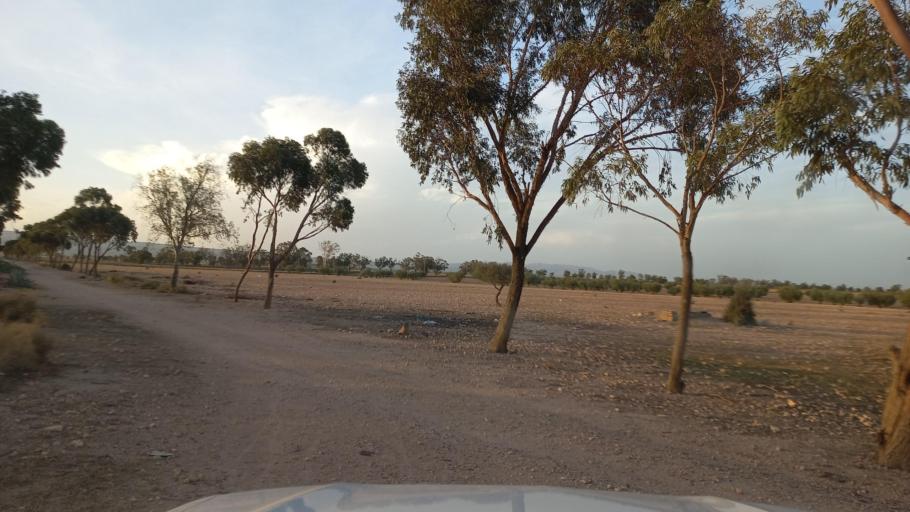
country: TN
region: Al Qasrayn
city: Kasserine
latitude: 35.2398
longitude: 8.9944
